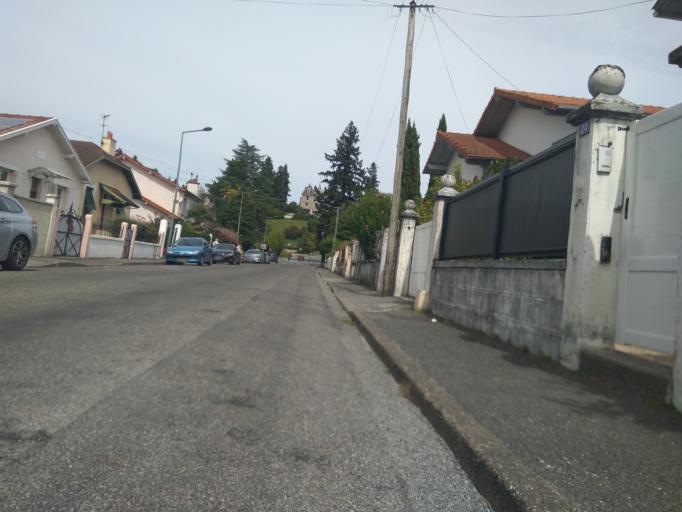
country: FR
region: Aquitaine
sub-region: Departement des Pyrenees-Atlantiques
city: Bizanos
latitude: 43.2937
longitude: -0.3538
